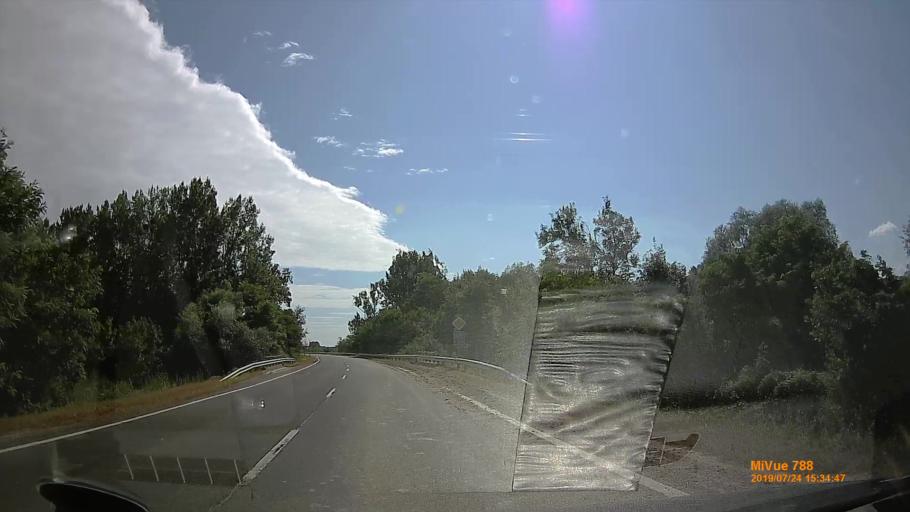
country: HU
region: Szabolcs-Szatmar-Bereg
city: Vasarosnameny
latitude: 48.1467
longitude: 22.3646
